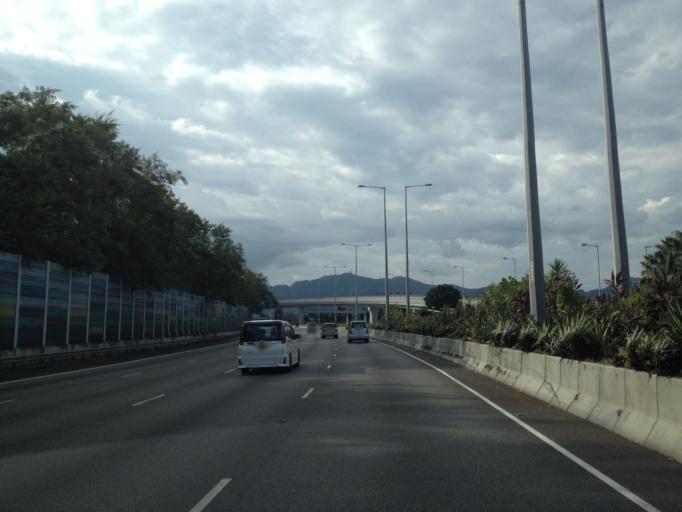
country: HK
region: Tai Po
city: Tai Po
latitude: 22.4346
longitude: 114.2000
